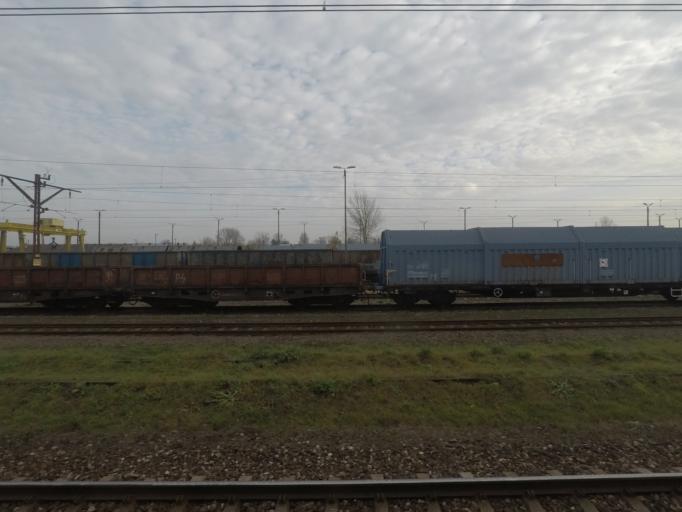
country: PL
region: Subcarpathian Voivodeship
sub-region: Powiat przemyski
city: Zurawica
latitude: 49.8301
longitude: 22.8358
